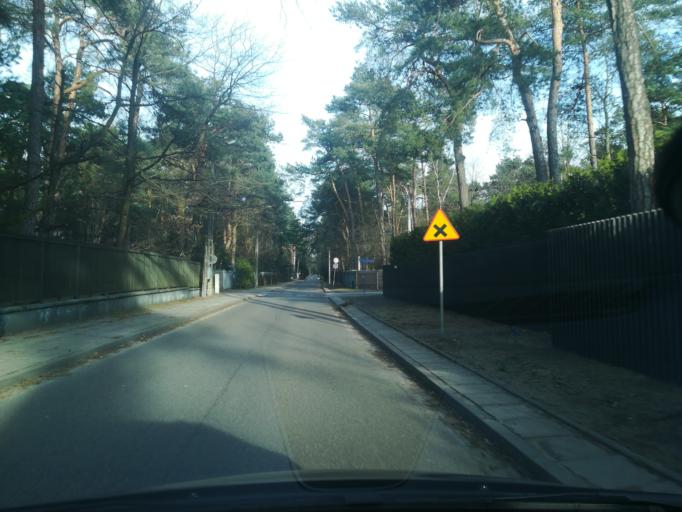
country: PL
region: Masovian Voivodeship
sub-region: Powiat piaseczynski
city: Konstancin-Jeziorna
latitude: 52.0744
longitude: 21.1085
